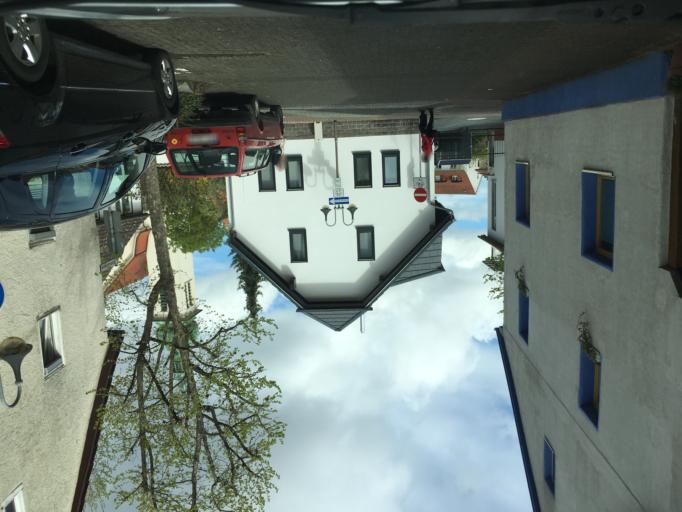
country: DE
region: Hesse
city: Obertshausen
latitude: 50.0711
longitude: 8.8491
